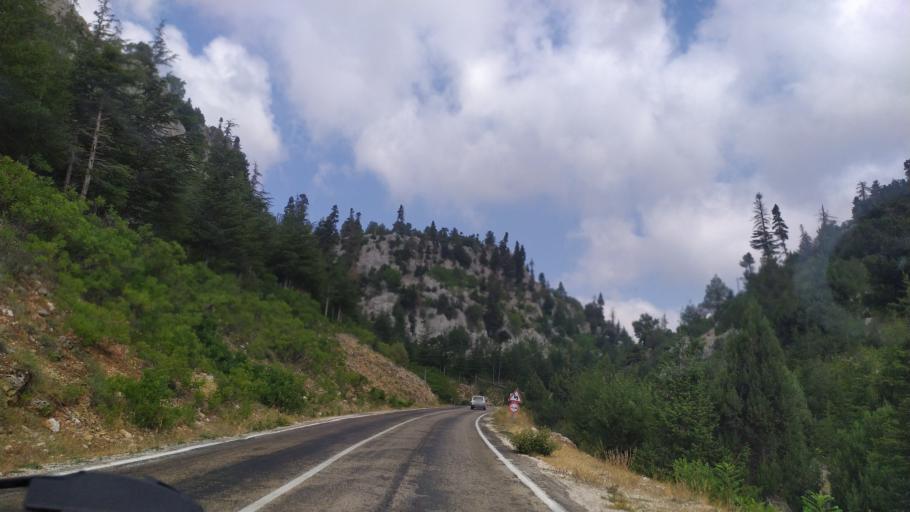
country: TR
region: Mersin
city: Kirobasi
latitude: 36.6037
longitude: 33.8876
